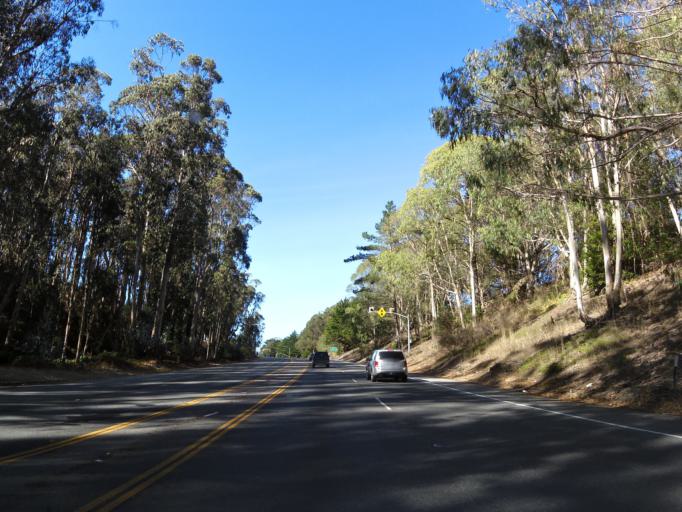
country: US
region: California
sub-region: San Mateo County
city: Pacifica
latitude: 37.6296
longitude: -122.4520
